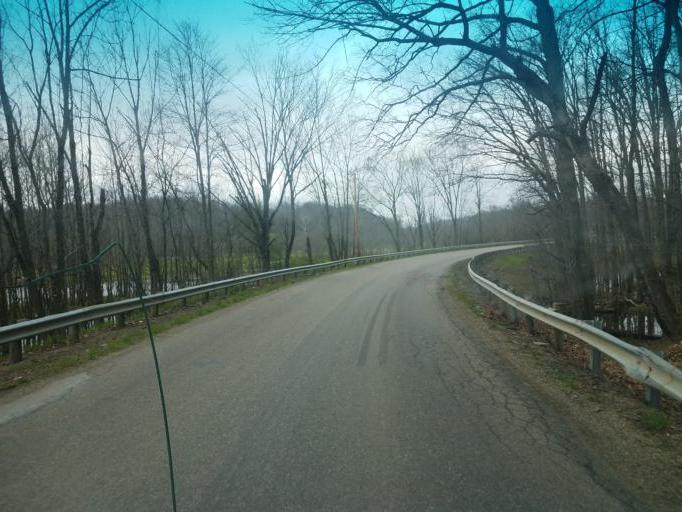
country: US
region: Ohio
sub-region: Stark County
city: Beach City
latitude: 40.5906
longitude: -81.6228
